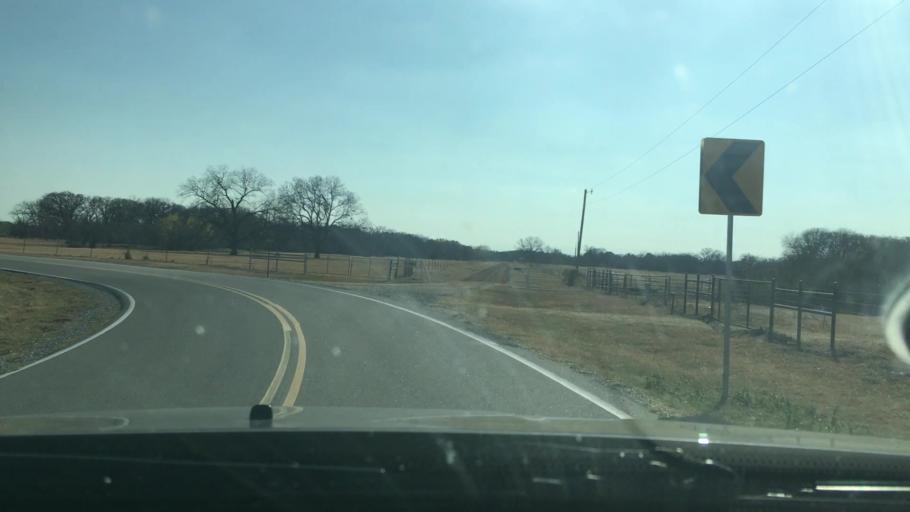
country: US
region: Oklahoma
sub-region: Marshall County
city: Oakland
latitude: 34.0262
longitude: -96.9348
